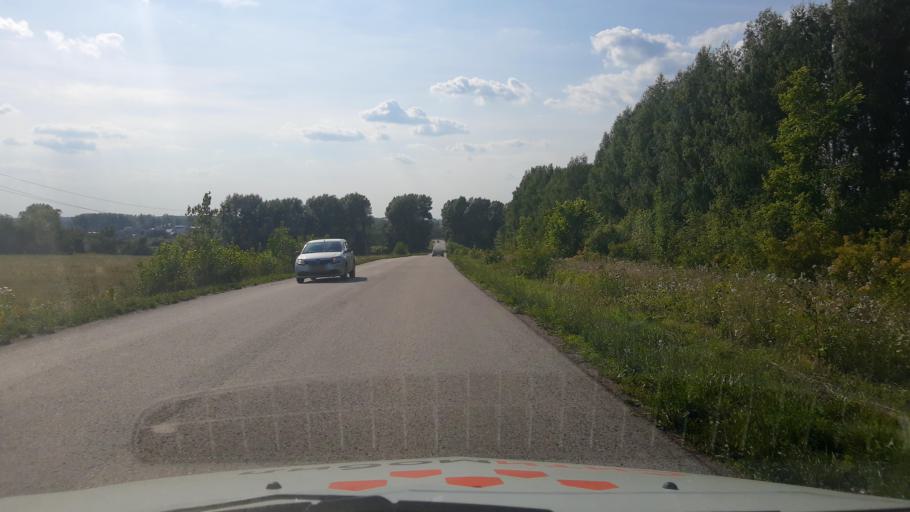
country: RU
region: Bashkortostan
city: Kabakovo
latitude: 54.6618
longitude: 56.1865
